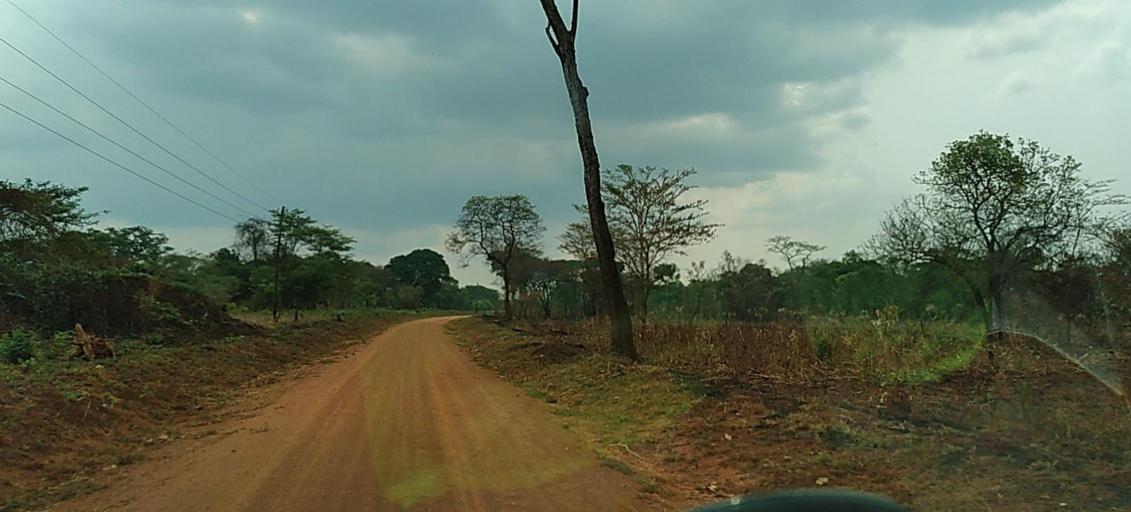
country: ZM
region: North-Western
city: Solwezi
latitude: -12.7838
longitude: 26.5003
